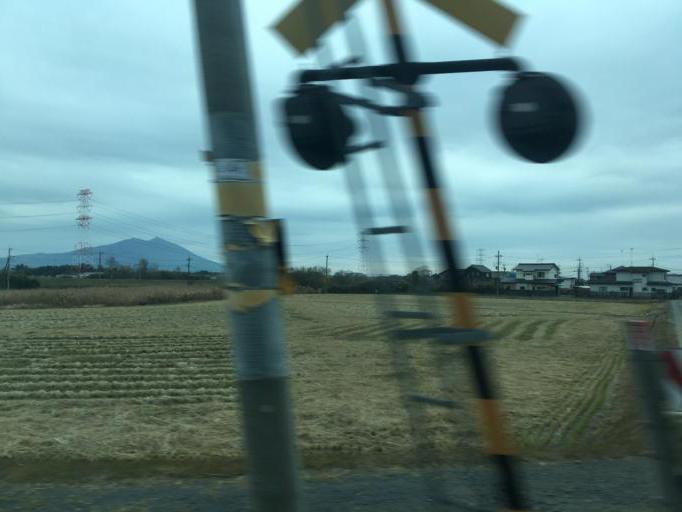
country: JP
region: Ibaraki
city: Shimodate
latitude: 36.3082
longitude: 139.9991
